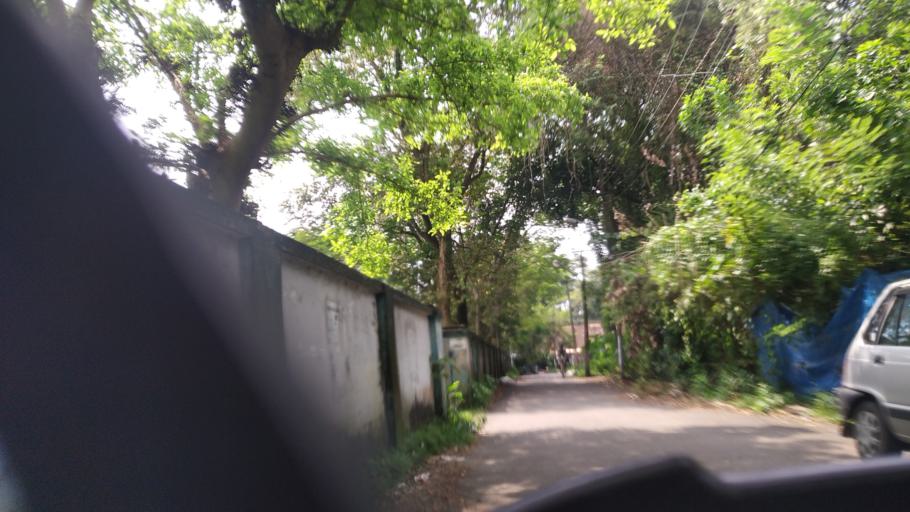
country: IN
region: Kerala
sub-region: Ernakulam
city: Cochin
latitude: 9.9949
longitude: 76.2856
